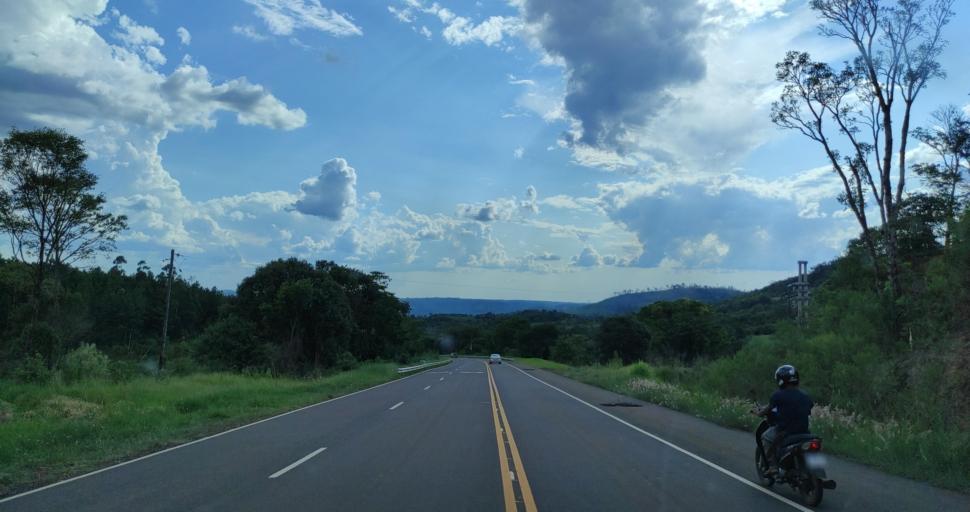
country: AR
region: Misiones
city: Bernardo de Irigoyen
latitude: -26.3045
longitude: -53.8169
